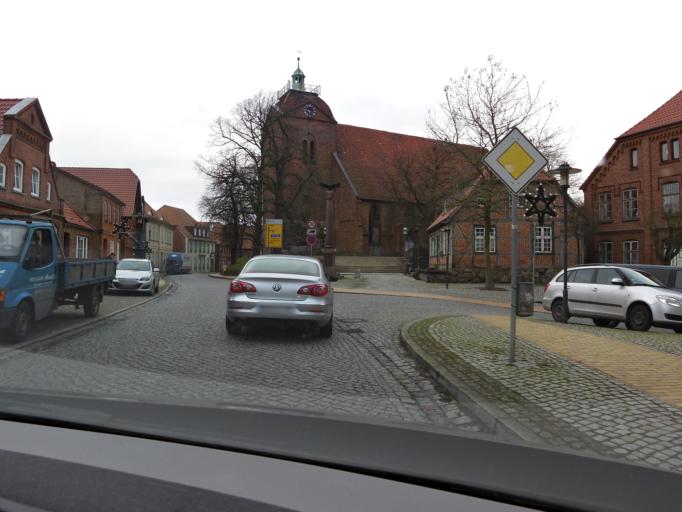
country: DE
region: Mecklenburg-Vorpommern
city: Dassow
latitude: 53.8443
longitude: 10.9326
